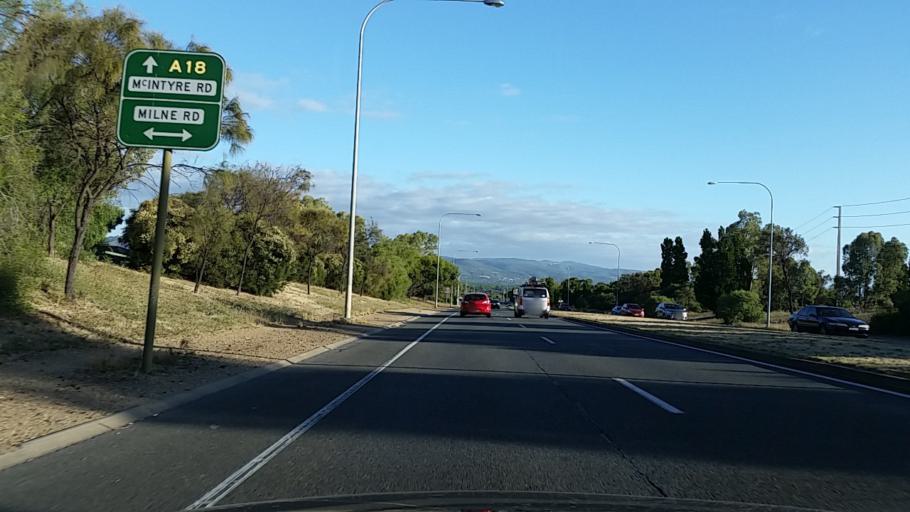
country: AU
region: South Australia
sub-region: Tea Tree Gully
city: Modbury
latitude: -34.8149
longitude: 138.6762
